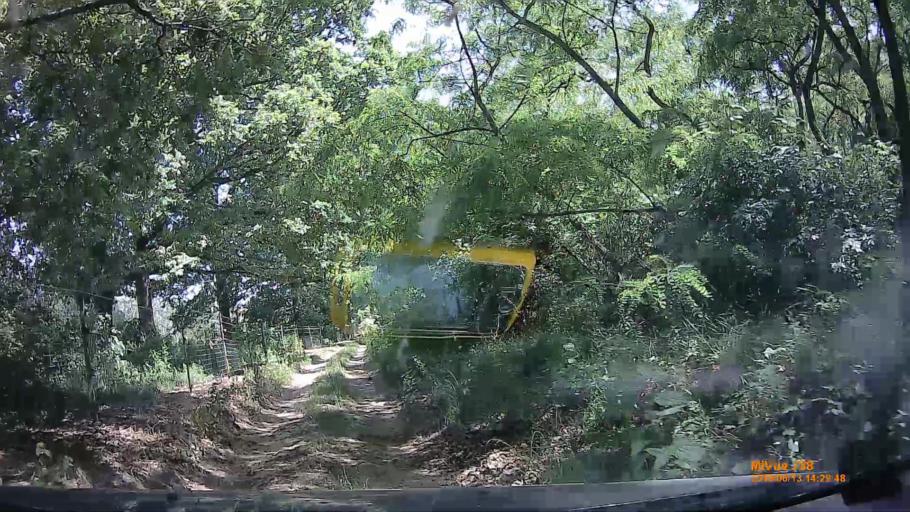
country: HU
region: Pest
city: Szada
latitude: 47.6028
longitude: 19.3052
